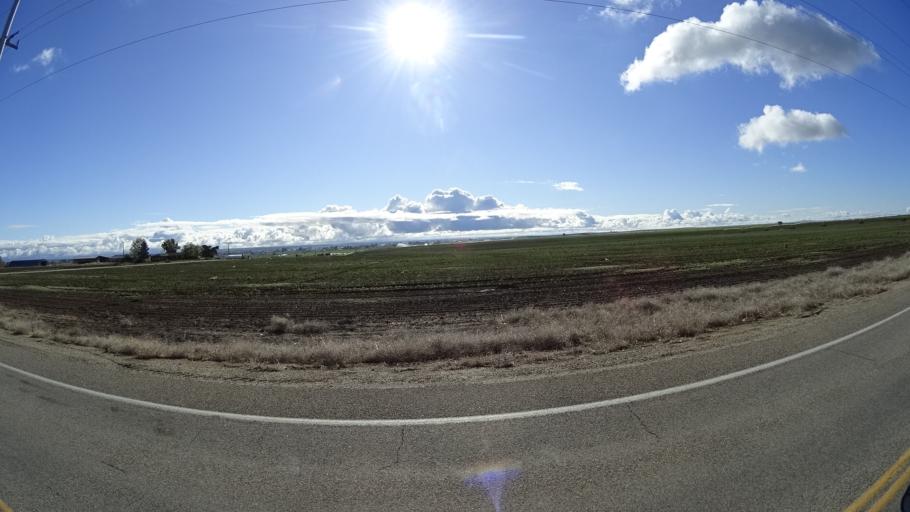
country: US
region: Idaho
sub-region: Ada County
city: Kuna
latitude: 43.4581
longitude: -116.4143
